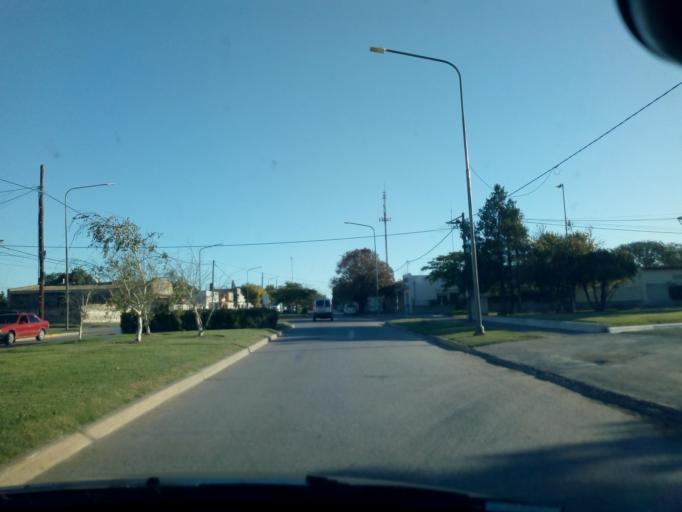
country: AR
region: Buenos Aires
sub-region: Partido de Loberia
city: Loberia
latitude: -38.1587
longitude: -58.7773
